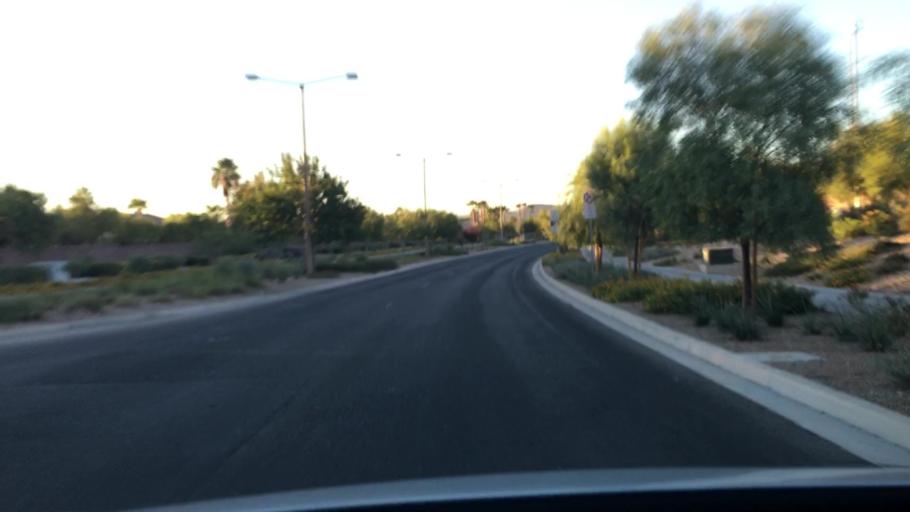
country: US
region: Nevada
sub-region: Clark County
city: Summerlin South
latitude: 36.1078
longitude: -115.3277
